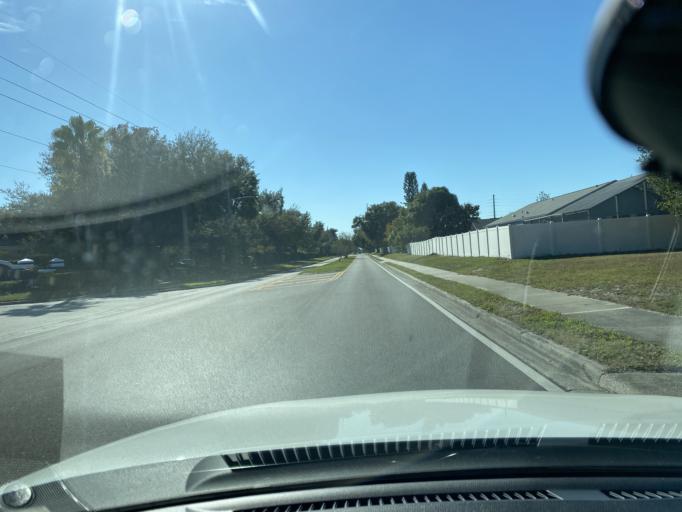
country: US
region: Florida
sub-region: Orange County
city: Conway
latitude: 28.5210
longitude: -81.3146
